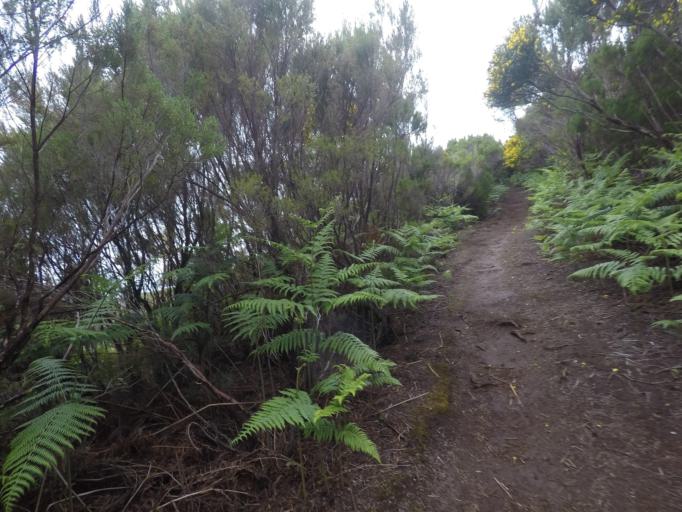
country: PT
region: Madeira
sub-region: Calheta
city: Arco da Calheta
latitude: 32.7779
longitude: -17.1327
